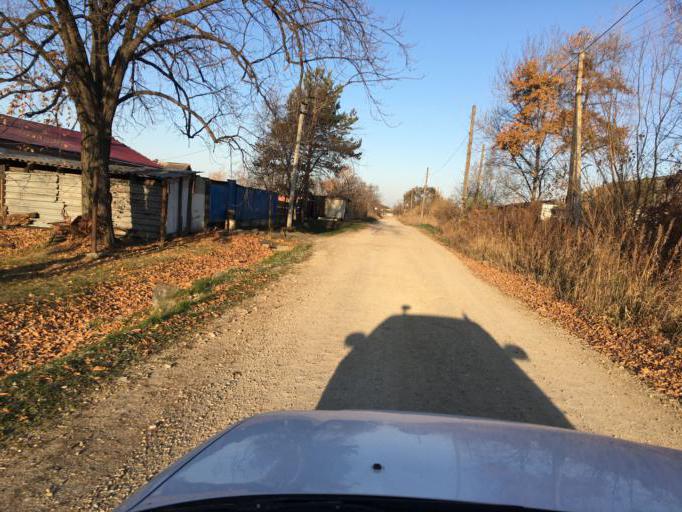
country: RU
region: Primorskiy
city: Lazo
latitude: 45.8633
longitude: 133.6442
